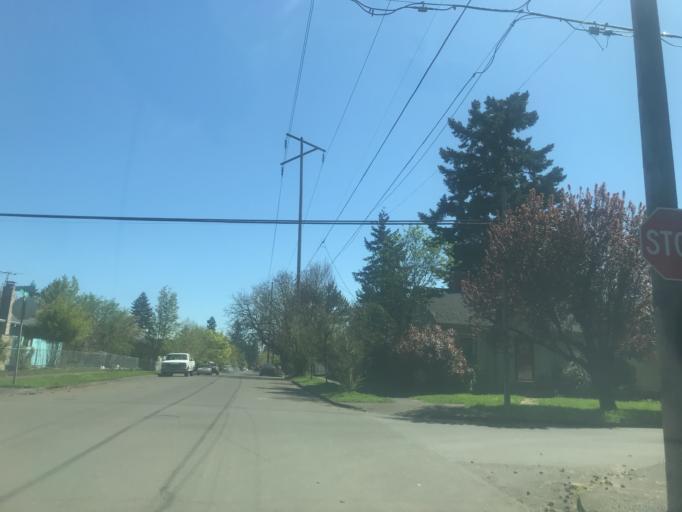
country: US
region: Oregon
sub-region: Multnomah County
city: Lents
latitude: 45.4817
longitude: -122.5998
